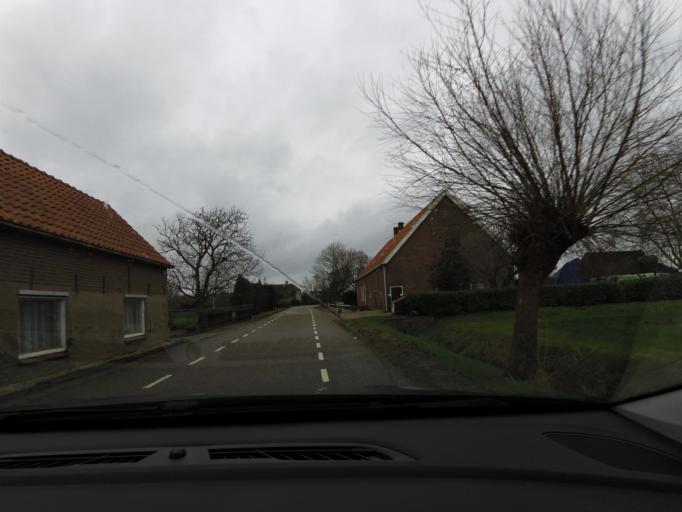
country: NL
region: North Brabant
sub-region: Gemeente Aalburg
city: Aalburg
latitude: 51.7608
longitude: 5.0907
